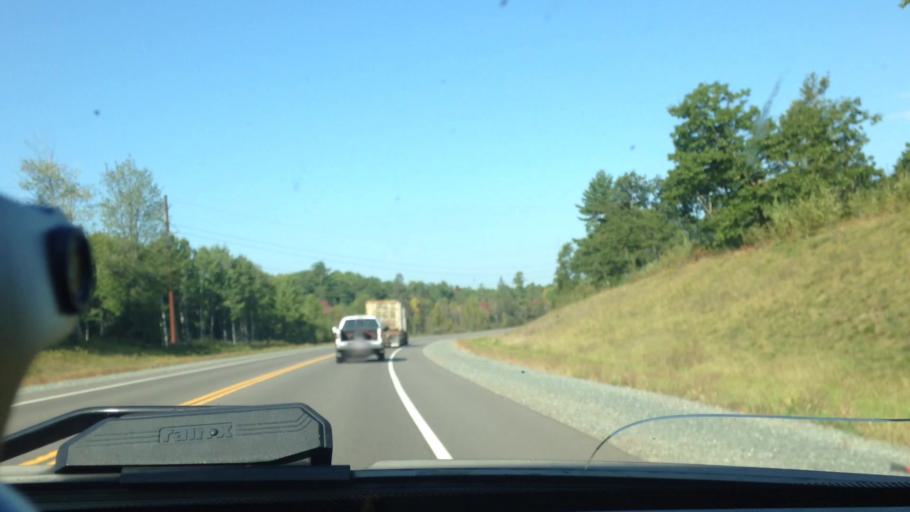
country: US
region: Michigan
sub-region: Dickinson County
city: Iron Mountain
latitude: 45.8760
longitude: -88.1136
